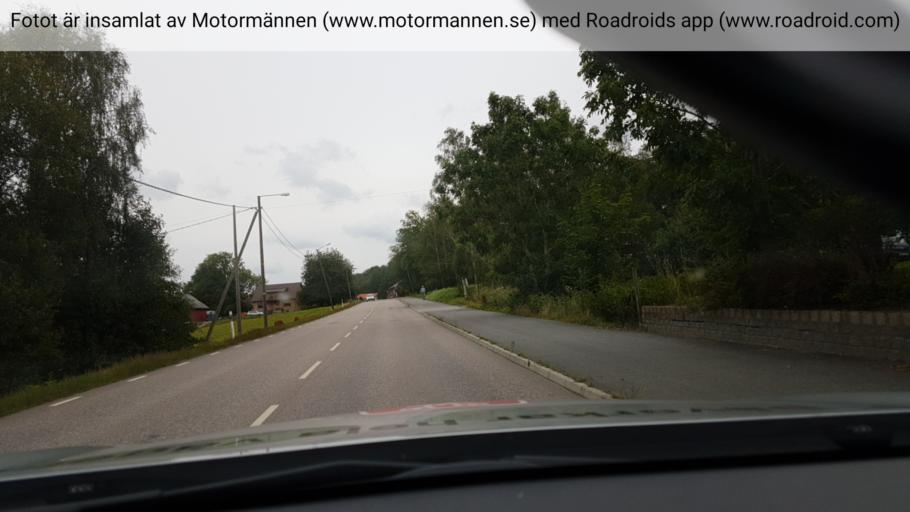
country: SE
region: Vaestra Goetaland
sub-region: Harryda Kommun
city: Molnlycke
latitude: 57.6004
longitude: 12.1853
